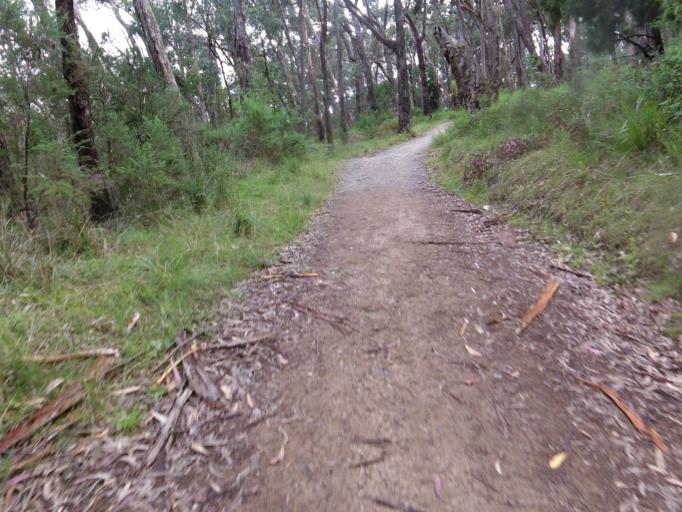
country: AU
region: Victoria
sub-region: Knox
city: The Basin
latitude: -37.8384
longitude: 145.3380
